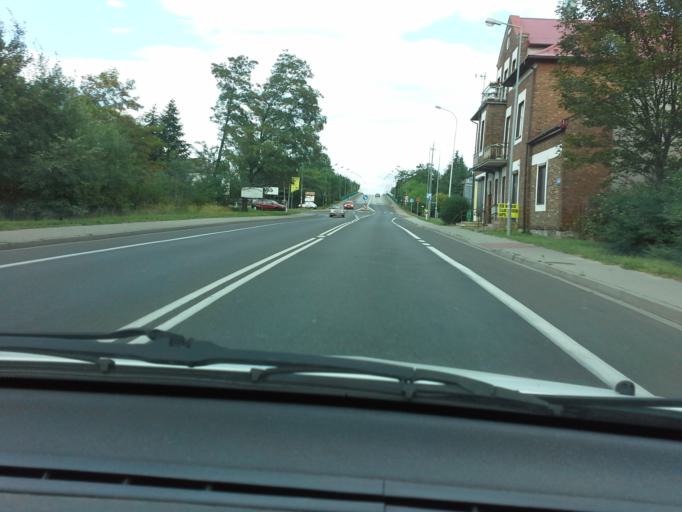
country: PL
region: Lesser Poland Voivodeship
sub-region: Powiat chrzanowski
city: Trzebinia
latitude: 50.1530
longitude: 19.4460
